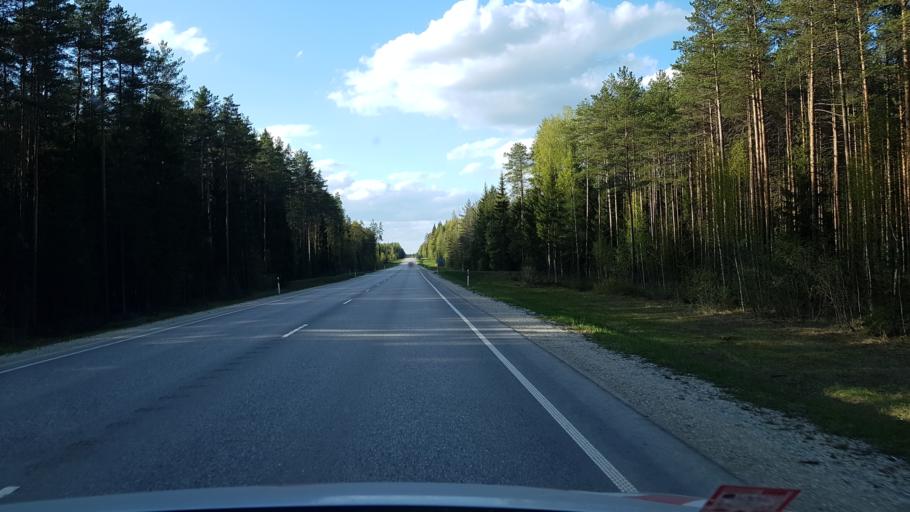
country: EE
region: Vorumaa
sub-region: Voru linn
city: Voru
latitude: 57.9422
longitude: 26.7963
